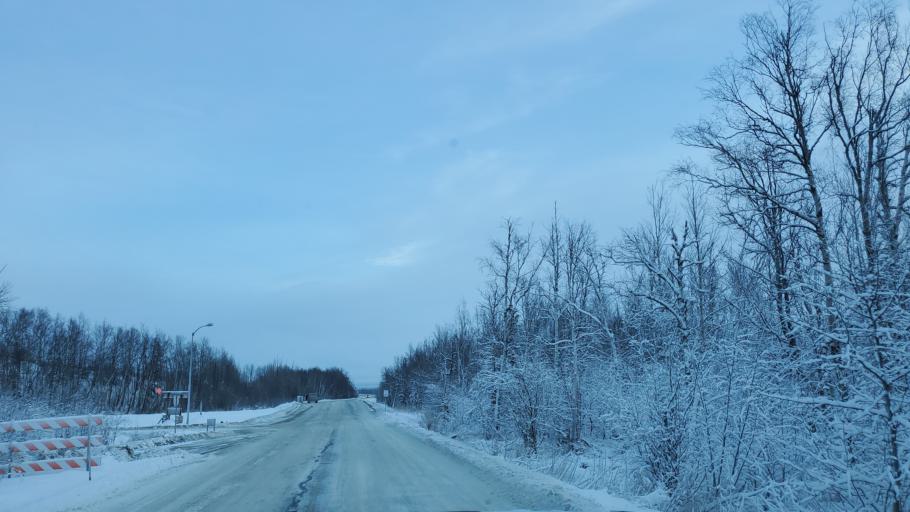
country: US
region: Alaska
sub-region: Matanuska-Susitna Borough
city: Gateway
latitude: 61.5506
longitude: -149.2939
